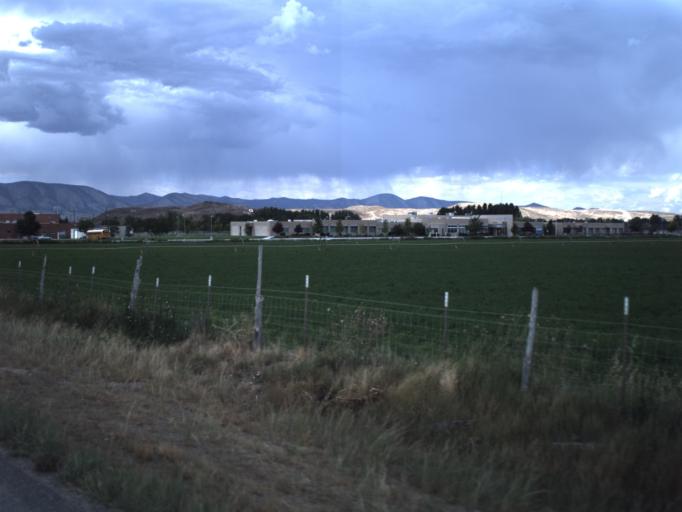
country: US
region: Utah
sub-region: Sanpete County
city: Gunnison
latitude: 39.1418
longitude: -111.8072
